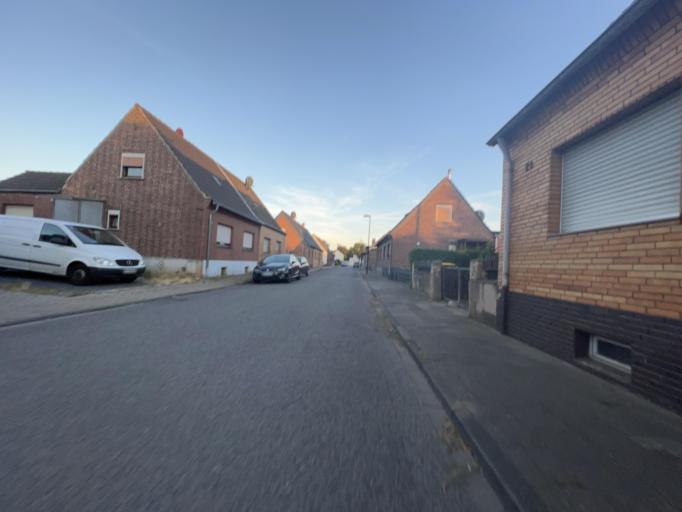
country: DE
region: North Rhine-Westphalia
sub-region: Regierungsbezirk Koln
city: Niederzier
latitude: 50.8500
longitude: 6.4270
